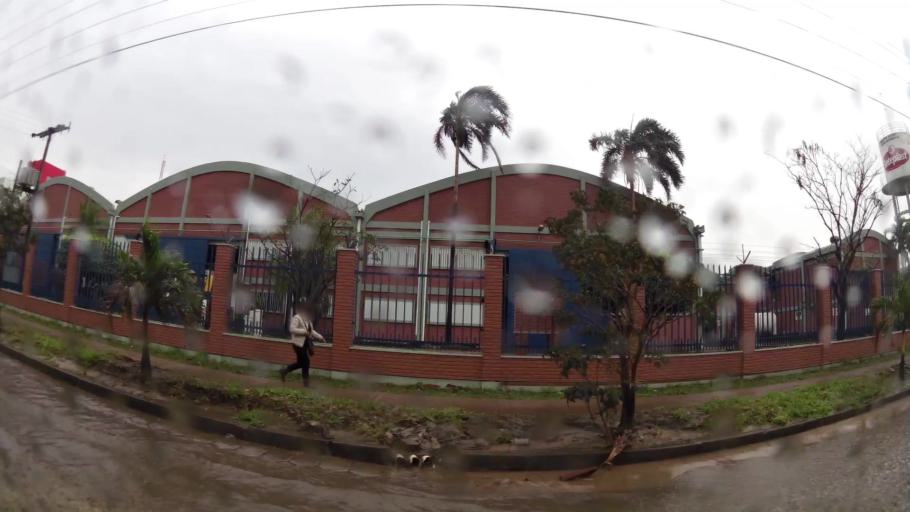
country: BO
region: Santa Cruz
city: Santa Cruz de la Sierra
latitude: -17.7579
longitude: -63.1381
